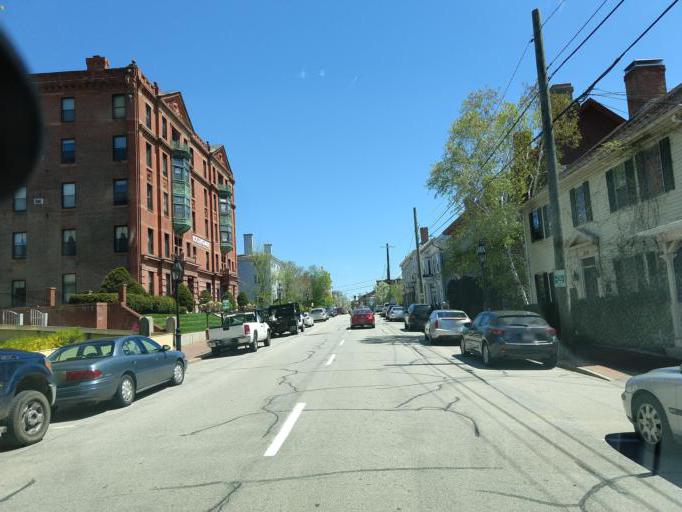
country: US
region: New Hampshire
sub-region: Rockingham County
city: Portsmouth
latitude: 43.0748
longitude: -70.7601
